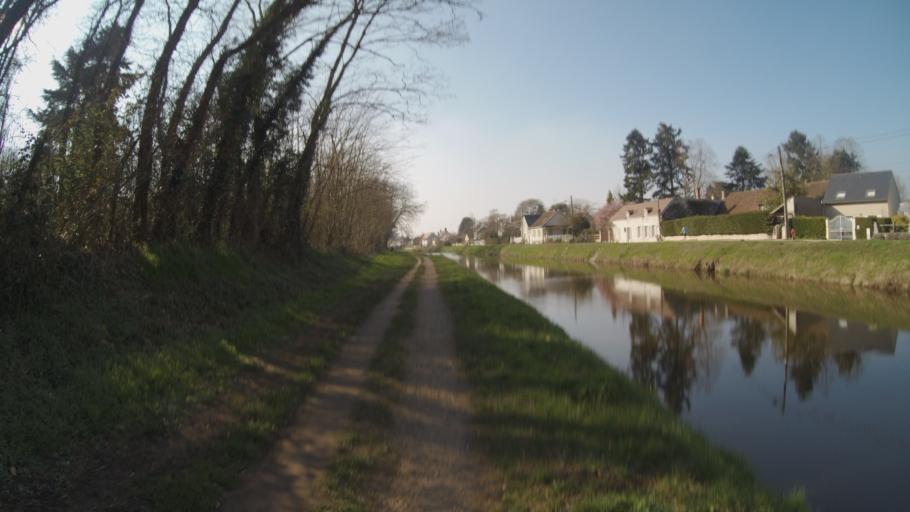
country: FR
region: Centre
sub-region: Departement du Loiret
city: Saint-Jean-de-Braye
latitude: 47.8967
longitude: 1.9970
